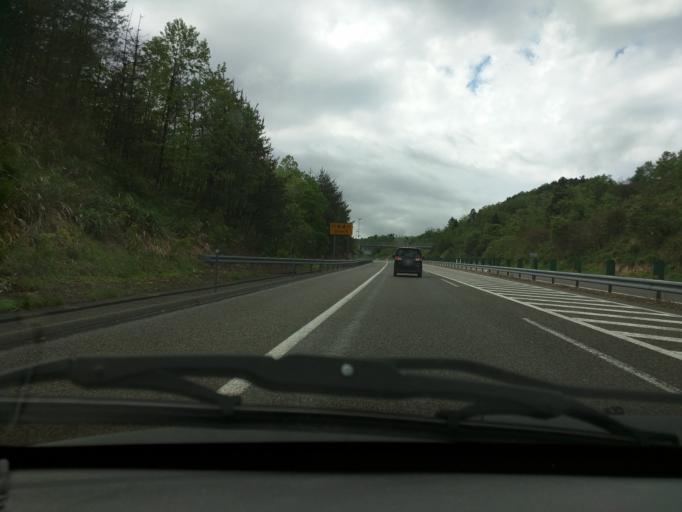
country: JP
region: Niigata
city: Joetsu
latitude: 37.1276
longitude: 138.2128
